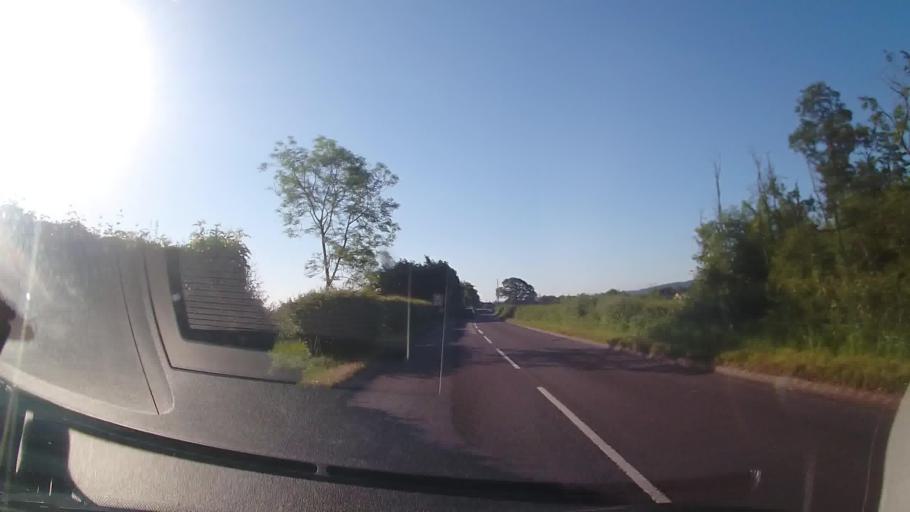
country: GB
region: England
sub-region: Shropshire
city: Withington
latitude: 52.7418
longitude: -2.5762
